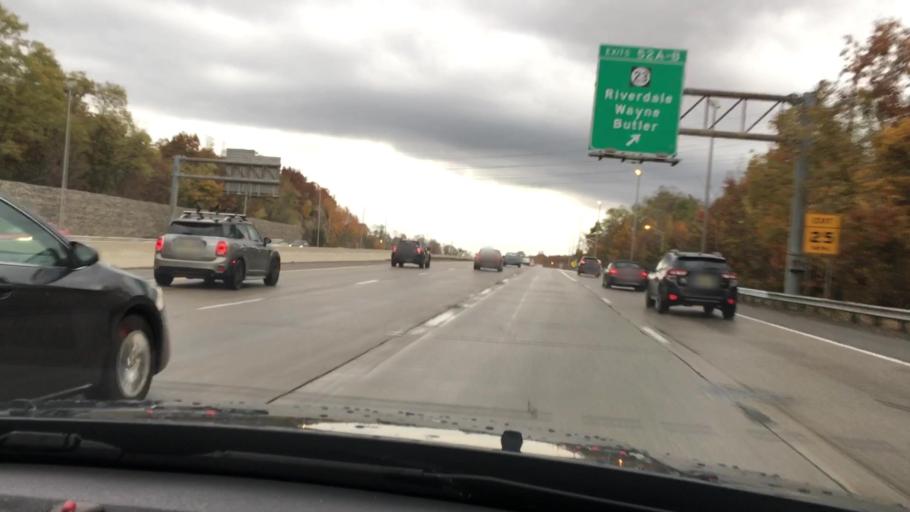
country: US
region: New Jersey
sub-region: Morris County
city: Riverdale
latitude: 40.9940
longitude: -74.3092
